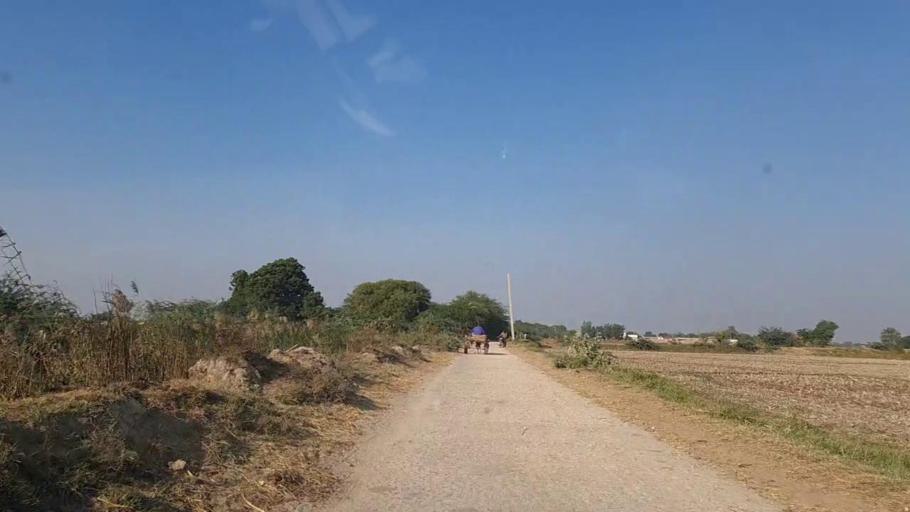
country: PK
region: Sindh
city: Thatta
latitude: 24.7549
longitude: 67.9612
